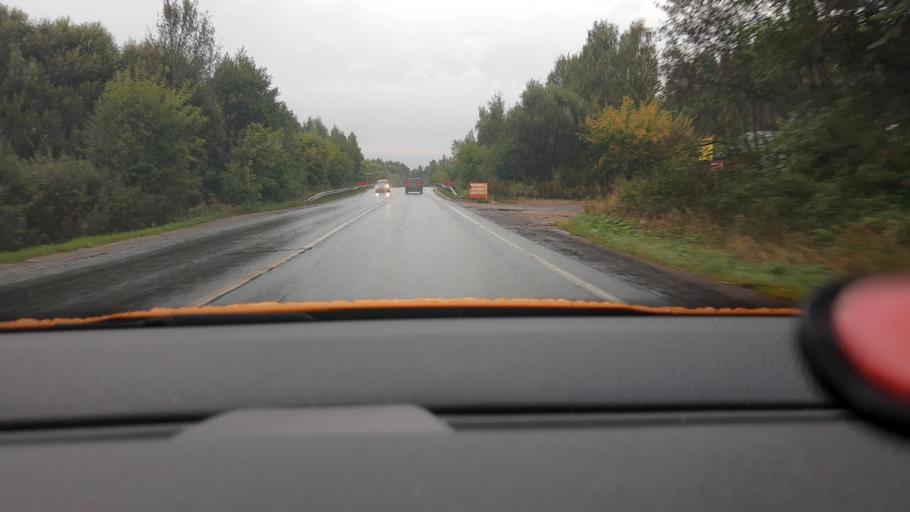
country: RU
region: Moskovskaya
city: Obukhovo
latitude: 55.8090
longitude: 38.2523
